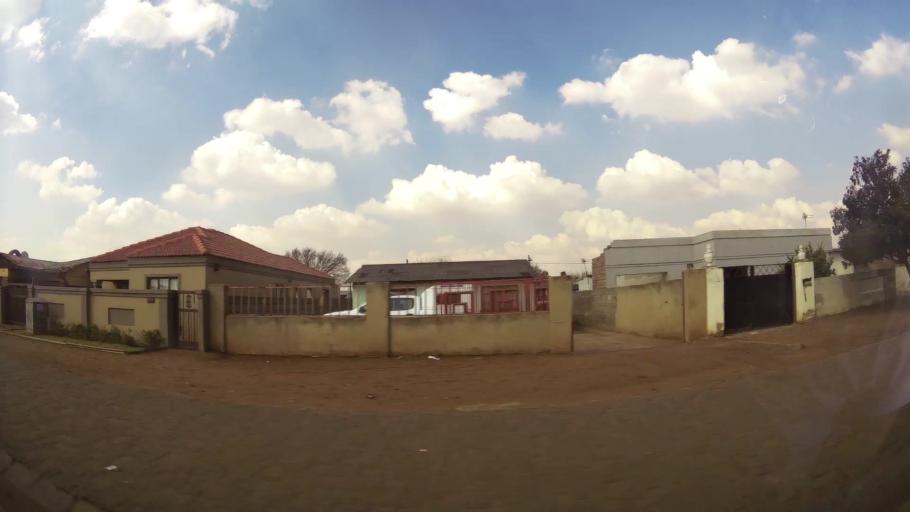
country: ZA
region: Gauteng
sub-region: Ekurhuleni Metropolitan Municipality
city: Germiston
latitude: -26.3430
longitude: 28.1381
